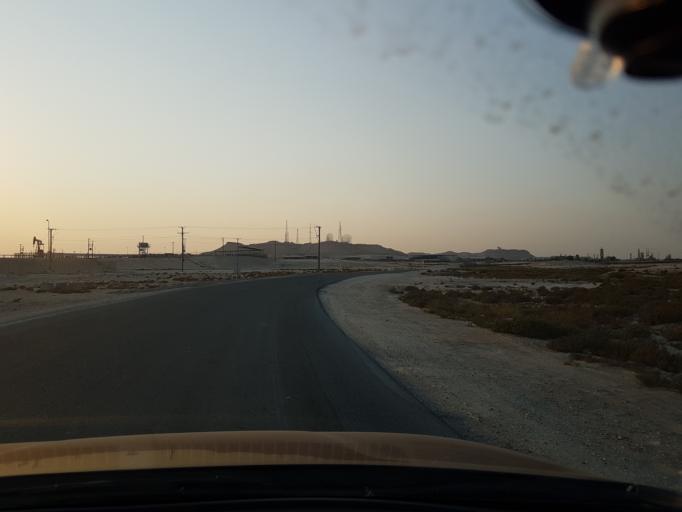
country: BH
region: Central Governorate
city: Dar Kulayb
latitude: 26.0191
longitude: 50.5584
